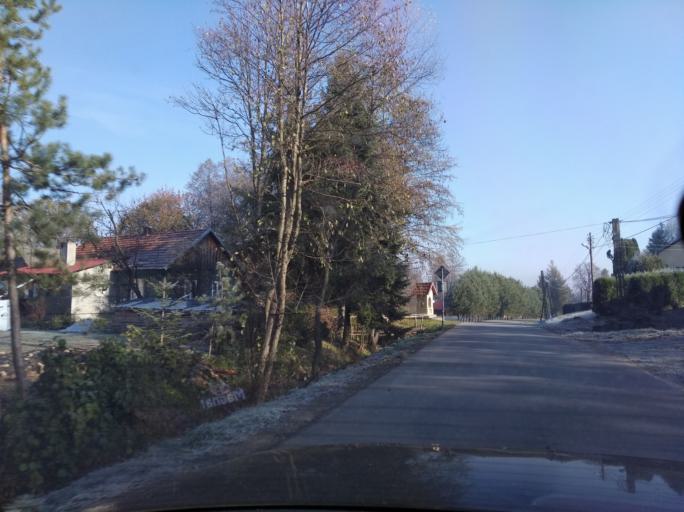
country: PL
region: Subcarpathian Voivodeship
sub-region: Powiat strzyzowski
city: Wysoka Strzyzowska
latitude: 49.8332
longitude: 21.7142
